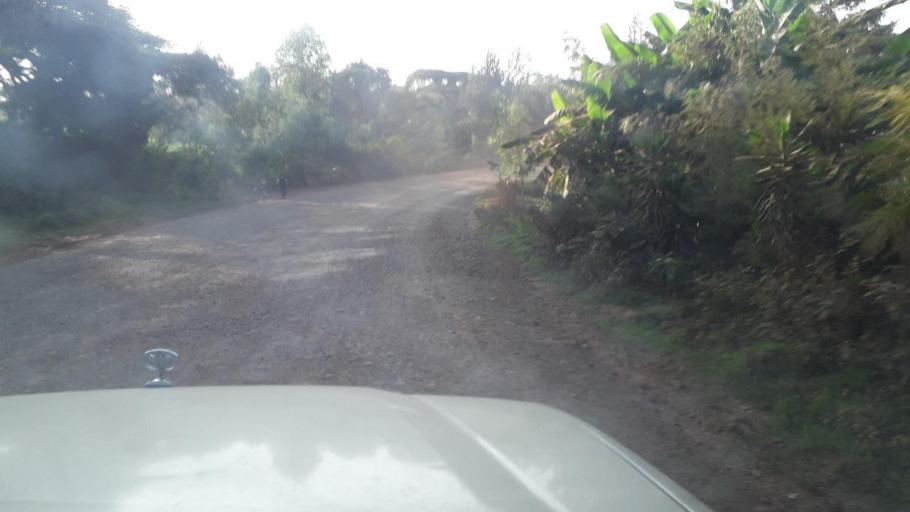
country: ET
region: Oromiya
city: Jima
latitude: 7.6019
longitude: 36.8431
